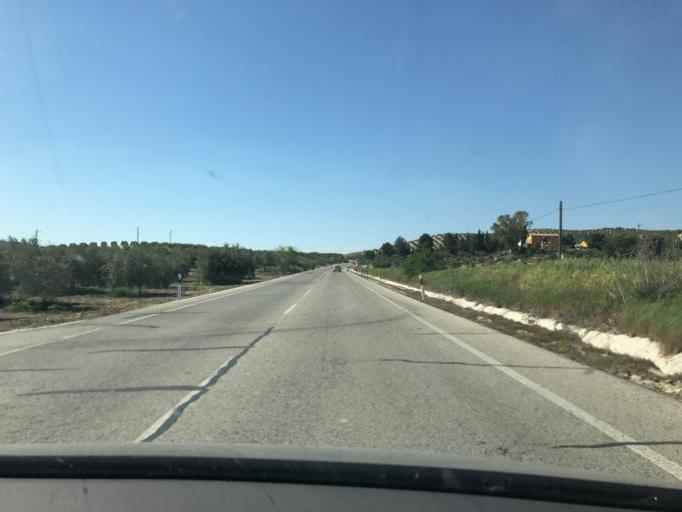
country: ES
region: Andalusia
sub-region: Province of Cordoba
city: Luque
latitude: 37.5878
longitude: -4.2935
